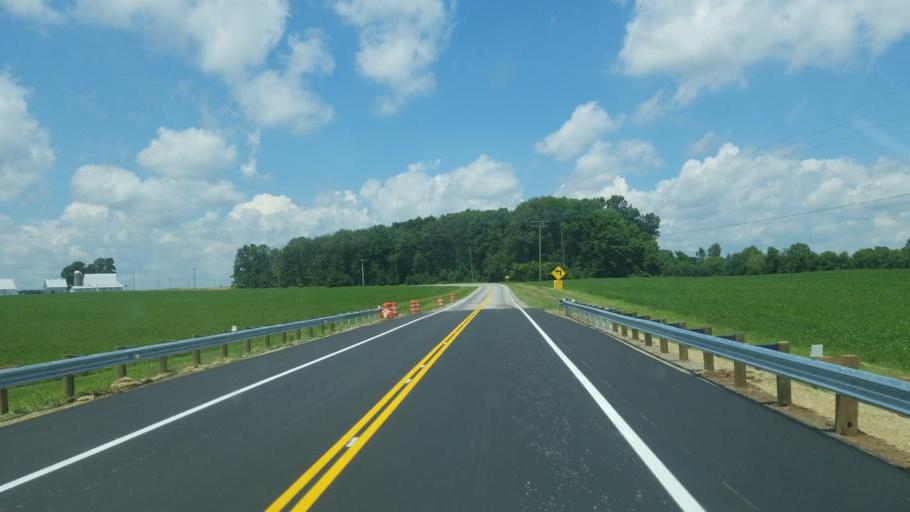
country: US
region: Ohio
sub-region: Highland County
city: Greenfield
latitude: 39.2410
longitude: -83.4320
